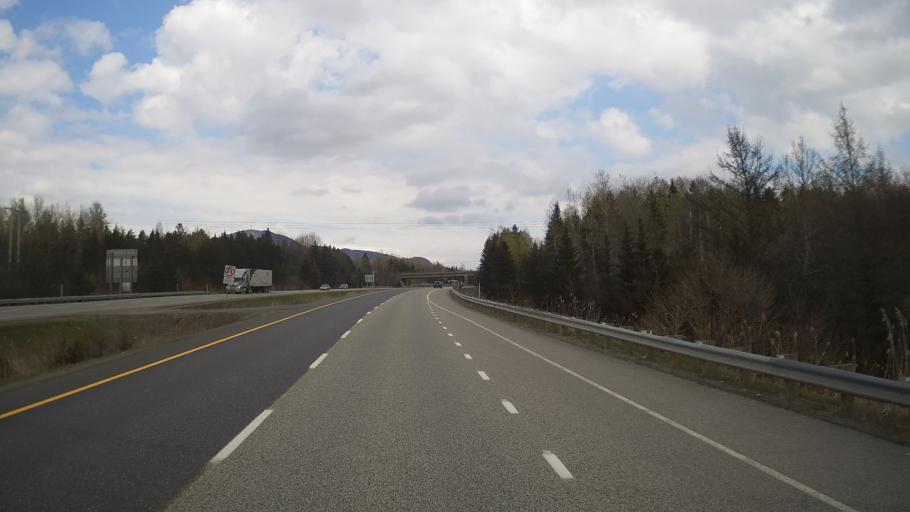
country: CA
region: Quebec
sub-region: Estrie
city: Magog
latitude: 45.2975
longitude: -72.3104
